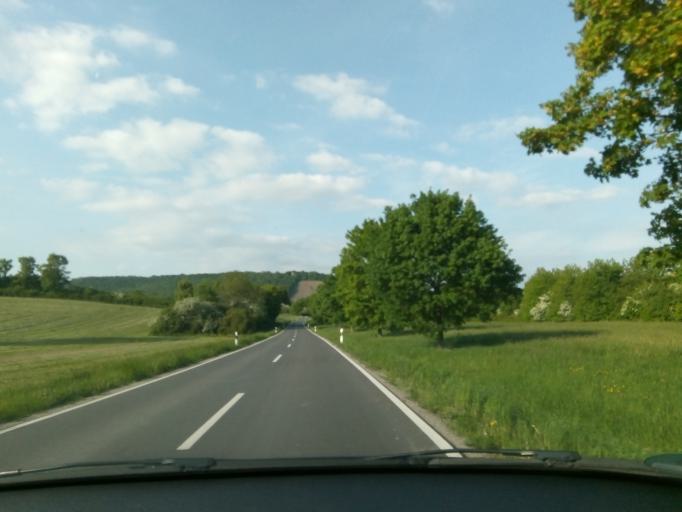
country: DE
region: Bavaria
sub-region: Regierungsbezirk Unterfranken
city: Oberschwarzach
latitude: 49.8634
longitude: 10.4193
